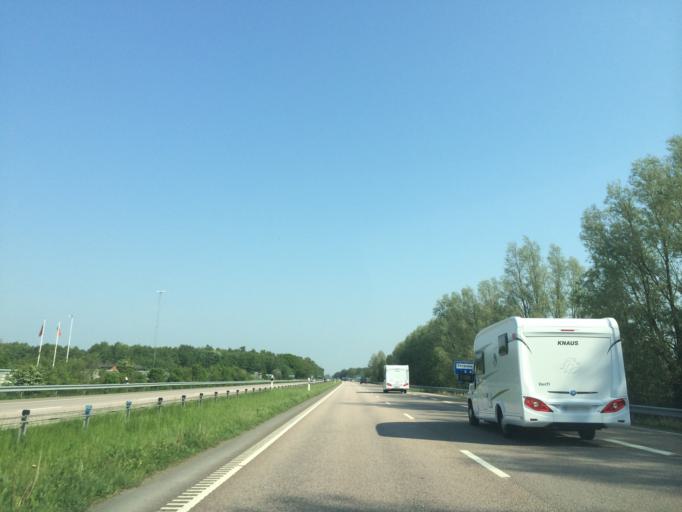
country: SE
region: Skane
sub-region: Helsingborg
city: Barslov
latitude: 56.0478
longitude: 12.7854
